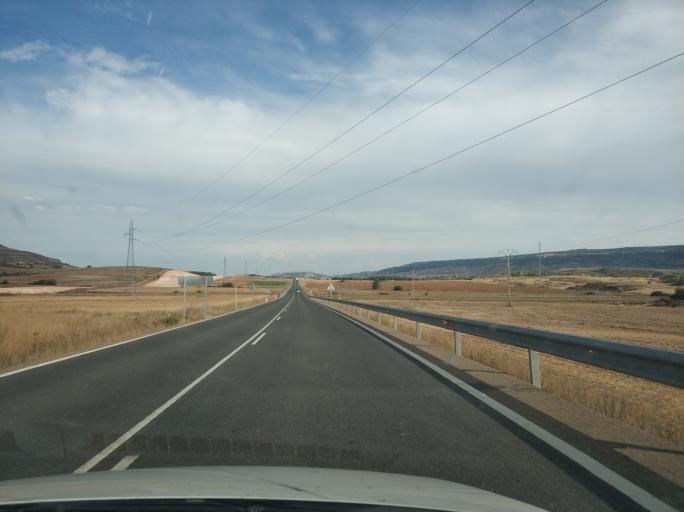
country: ES
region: Castille and Leon
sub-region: Provincia de Palencia
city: Pomar de Valdivia
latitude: 42.7527
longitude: -4.1743
